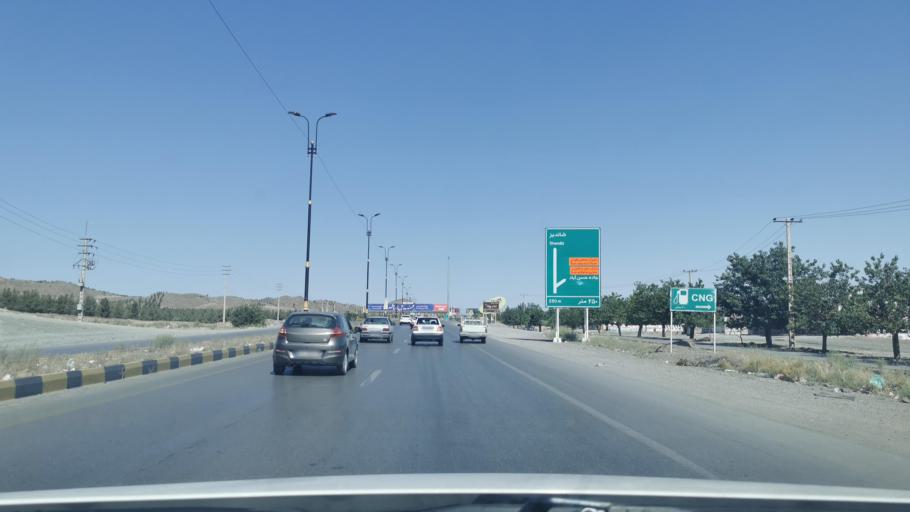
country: IR
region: Razavi Khorasan
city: Torqabeh
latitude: 36.4029
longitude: 59.3851
